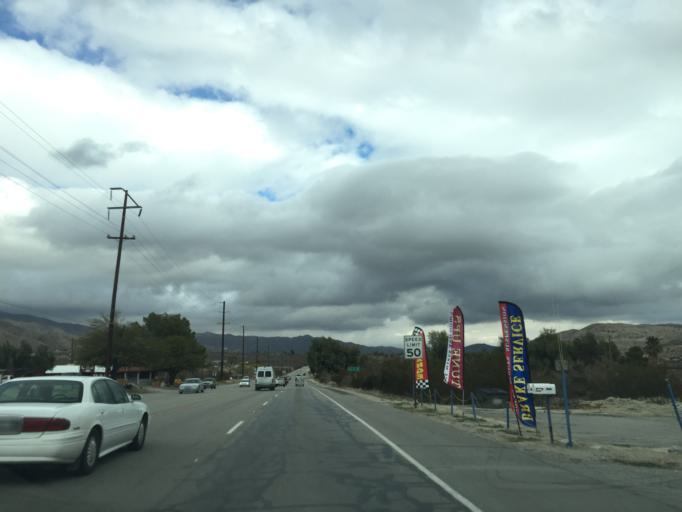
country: US
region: California
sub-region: San Bernardino County
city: Morongo Valley
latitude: 34.0512
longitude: -116.5760
